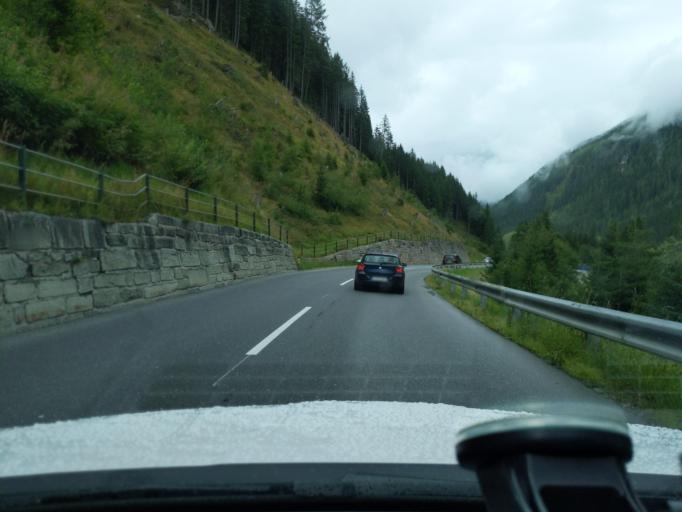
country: AT
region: Tyrol
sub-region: Politischer Bezirk Innsbruck Land
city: Schmirn
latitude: 47.1185
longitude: 11.6877
